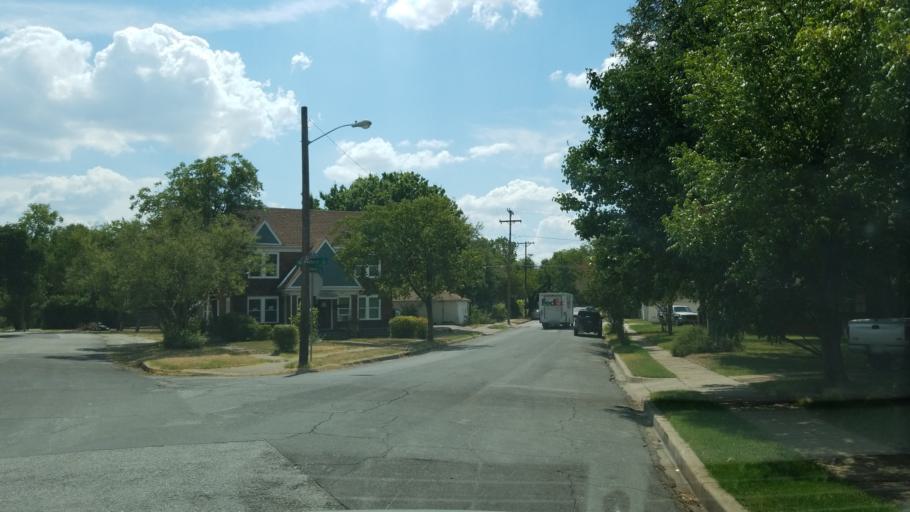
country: US
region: Texas
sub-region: Dallas County
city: Cockrell Hill
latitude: 32.7546
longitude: -96.8440
